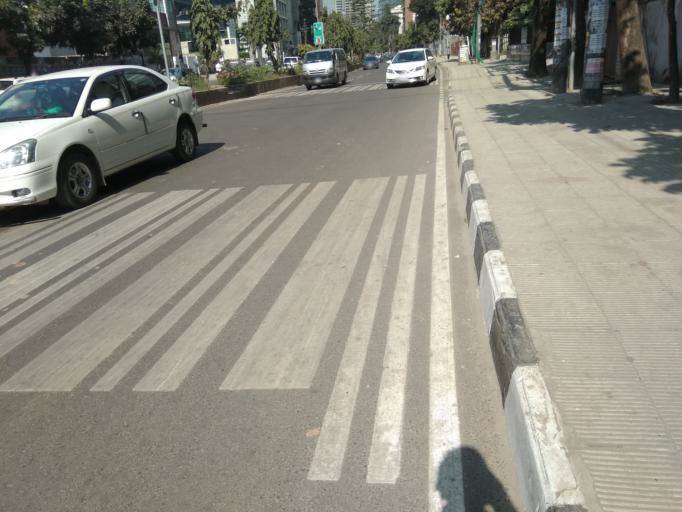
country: BD
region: Dhaka
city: Paltan
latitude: 23.7862
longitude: 90.4170
